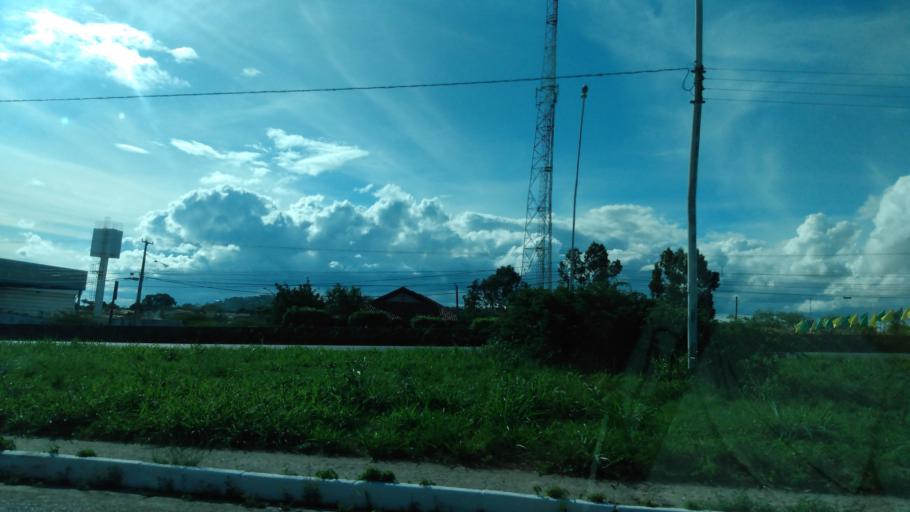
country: ET
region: Oromiya
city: Gore
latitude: 8.2012
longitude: 35.5911
